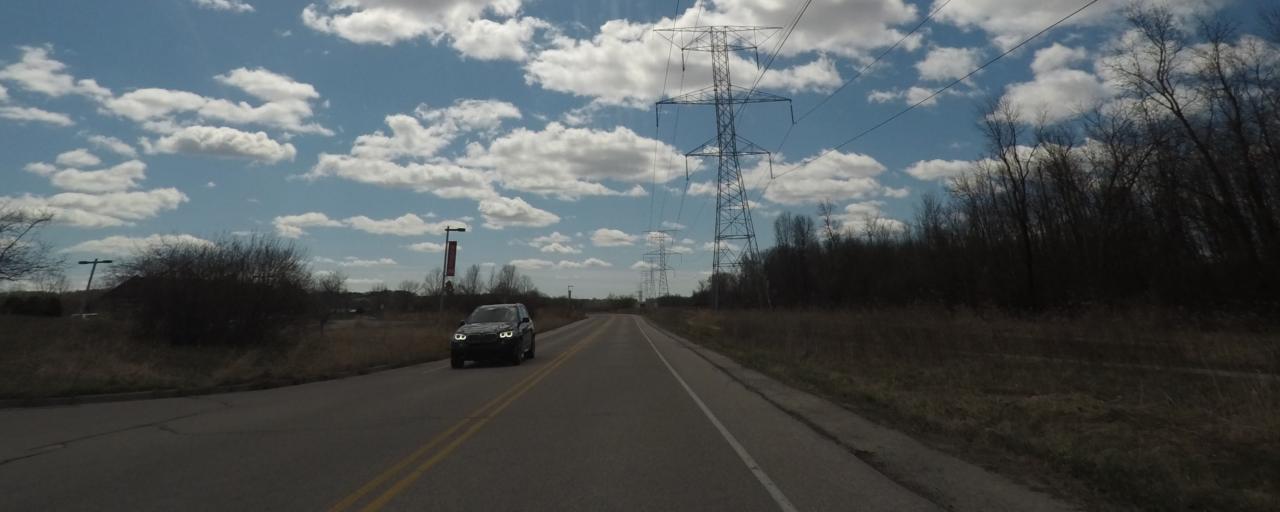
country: US
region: Wisconsin
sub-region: Waukesha County
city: Brookfield
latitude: 43.0779
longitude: -88.1607
